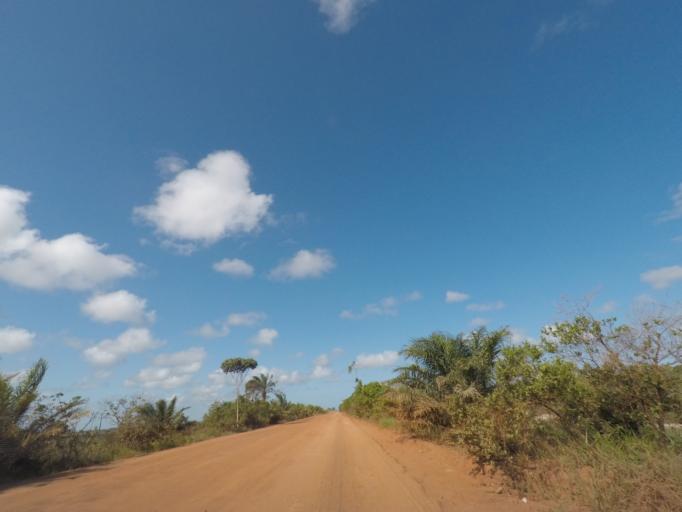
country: BR
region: Bahia
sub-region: Marau
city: Marau
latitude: -14.1786
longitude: -39.0219
